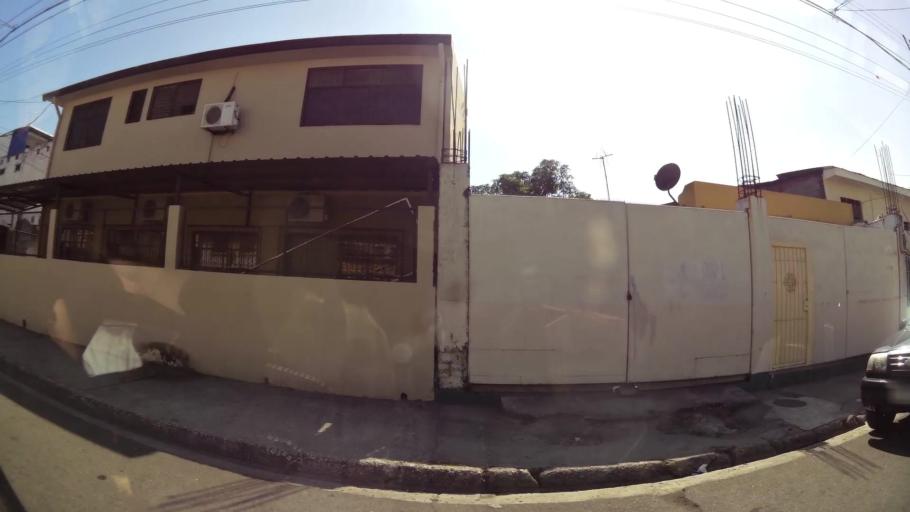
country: EC
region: Guayas
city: Guayaquil
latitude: -2.2142
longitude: -79.8977
